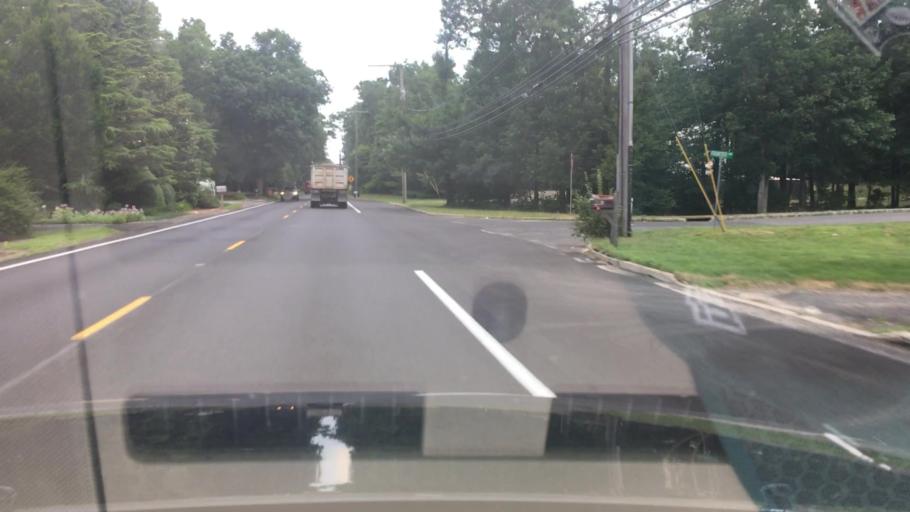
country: US
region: New Jersey
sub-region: Ocean County
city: Vista Center
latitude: 40.0946
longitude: -74.3848
